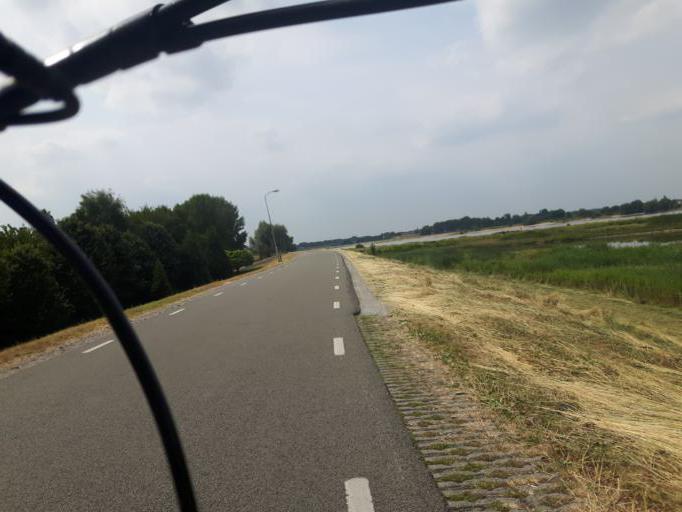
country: NL
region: Gelderland
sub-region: Gemeente Zaltbommel
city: Nederhemert
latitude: 51.8102
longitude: 5.1481
